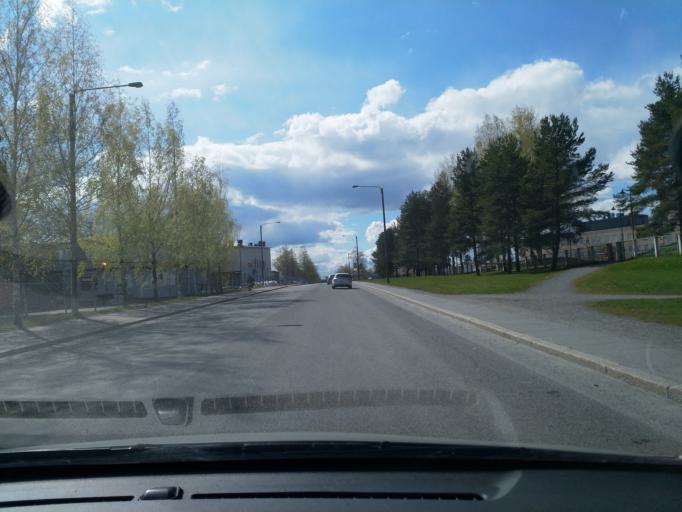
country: FI
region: Pirkanmaa
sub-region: Tampere
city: Tampere
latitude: 61.4825
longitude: 23.7936
